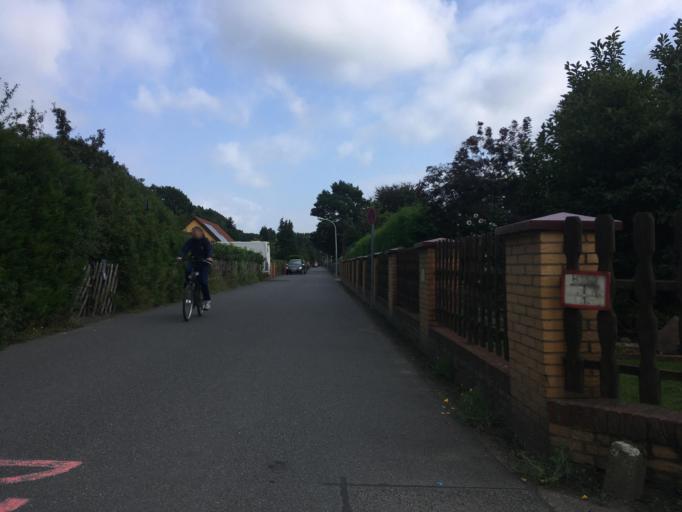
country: DE
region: Berlin
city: Haselhorst
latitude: 52.5556
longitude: 13.2447
